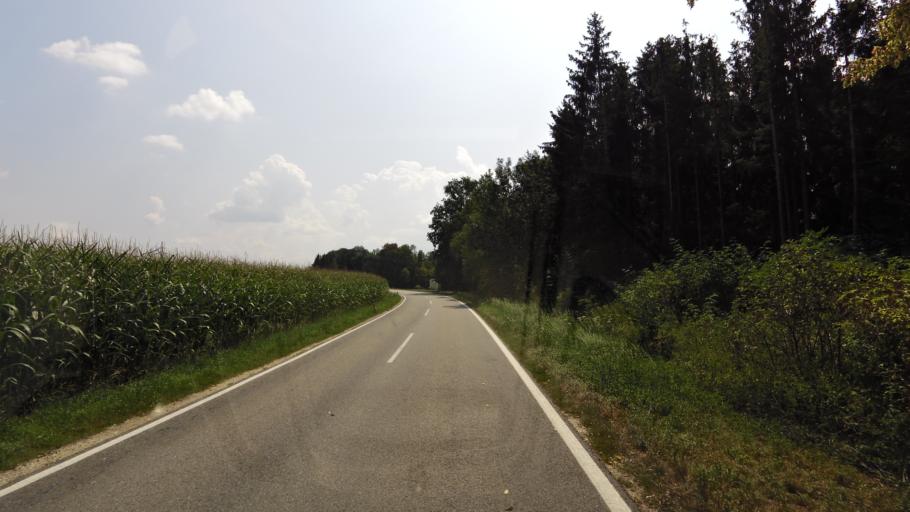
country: AT
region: Upper Austria
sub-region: Politischer Bezirk Ried im Innkreis
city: Waldzell
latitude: 48.1829
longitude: 13.3965
